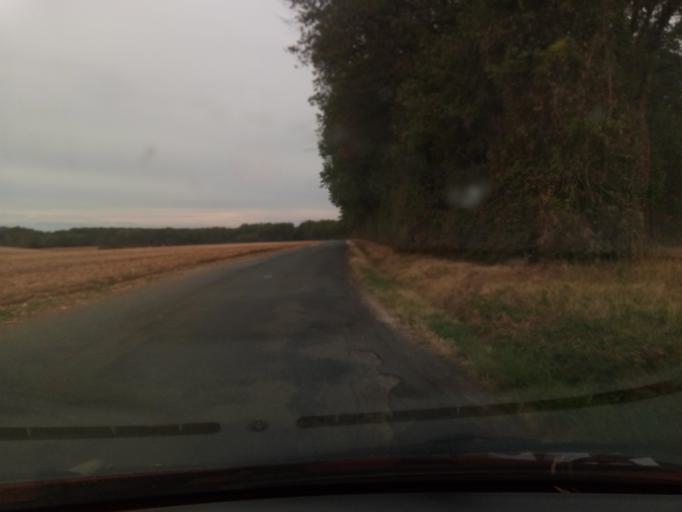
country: FR
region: Poitou-Charentes
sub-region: Departement de la Vienne
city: Saint-Savin
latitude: 46.5328
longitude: 0.7798
